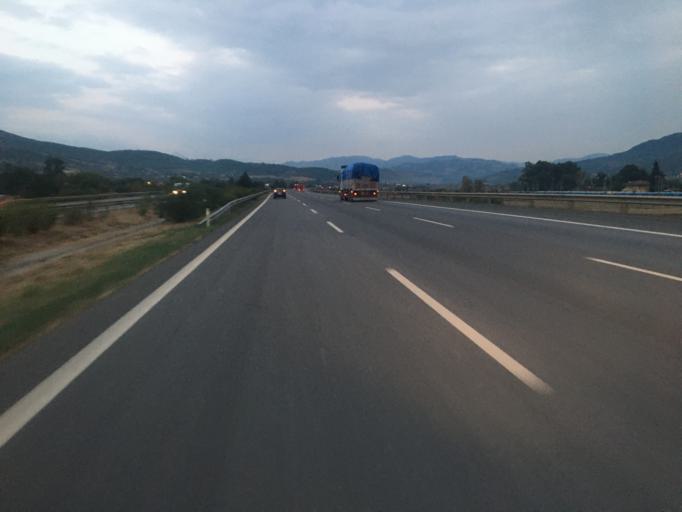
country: TR
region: Osmaniye
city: Osmaniye
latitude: 37.1360
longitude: 36.3132
